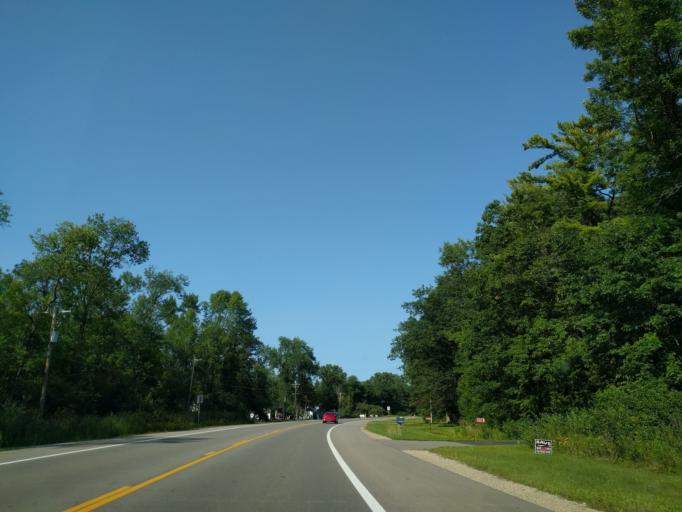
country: US
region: Michigan
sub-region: Menominee County
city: Menominee
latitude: 45.1494
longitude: -87.6024
